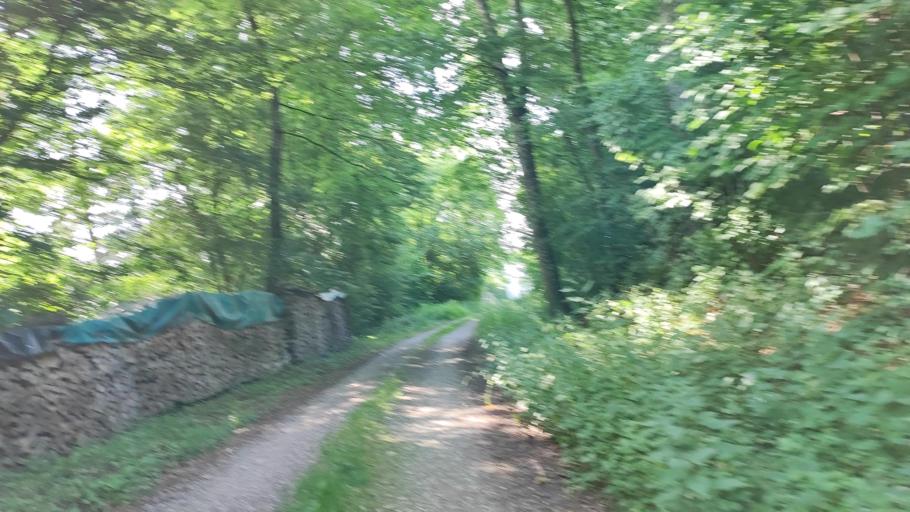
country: DE
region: Bavaria
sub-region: Swabia
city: Altenmunster
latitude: 48.4755
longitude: 10.5835
